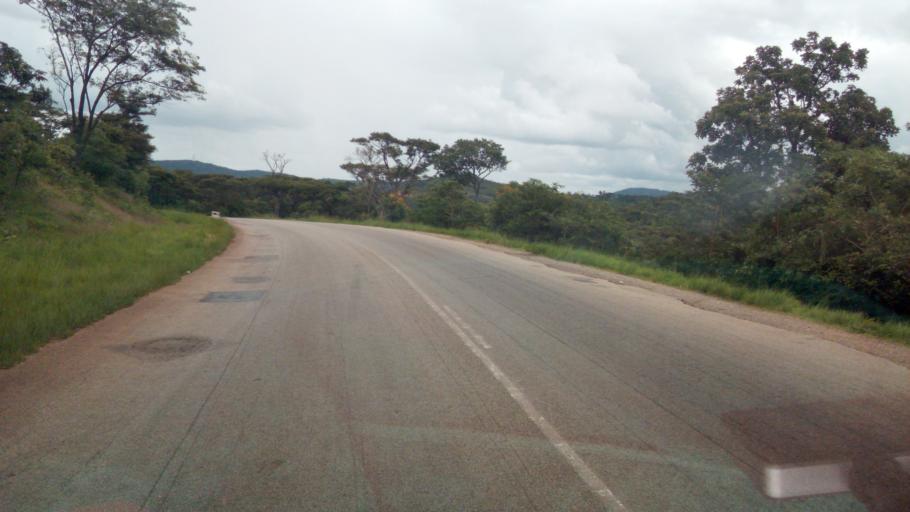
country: ZW
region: Mashonaland Central
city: Mazowe
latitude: -17.6366
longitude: 30.9770
